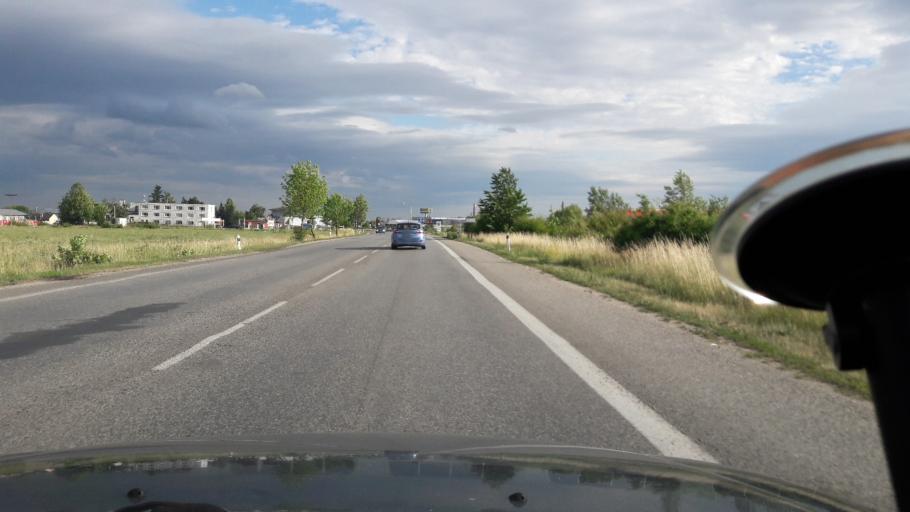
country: SK
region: Bratislavsky
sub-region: Okres Pezinok
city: Pezinok
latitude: 48.2950
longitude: 17.2810
